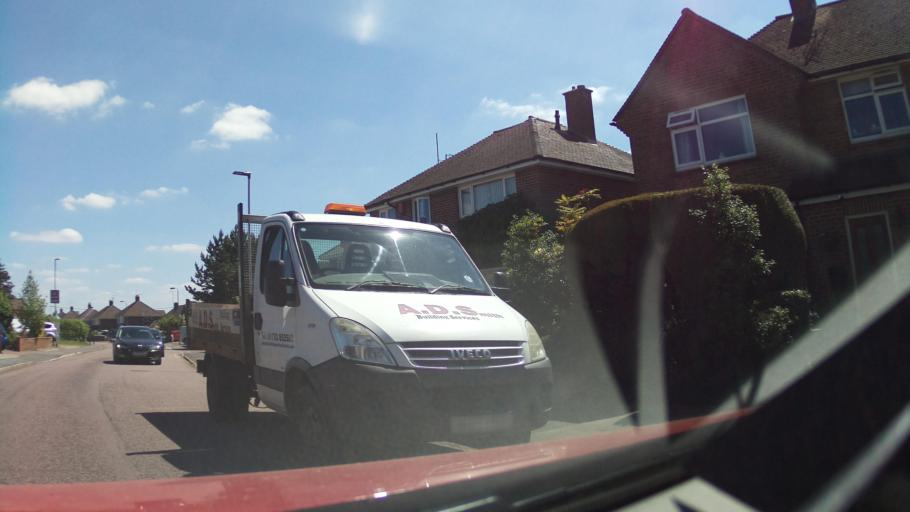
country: GB
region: England
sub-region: Wiltshire
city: Royal Wootton Bassett
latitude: 51.5458
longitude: -1.8948
